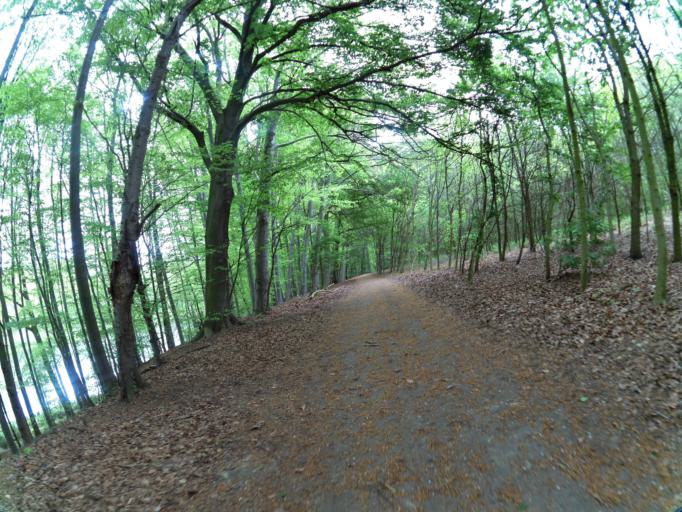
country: NL
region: Limburg
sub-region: Gemeente Kerkrade
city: Kerkrade
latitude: 50.8800
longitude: 6.0293
